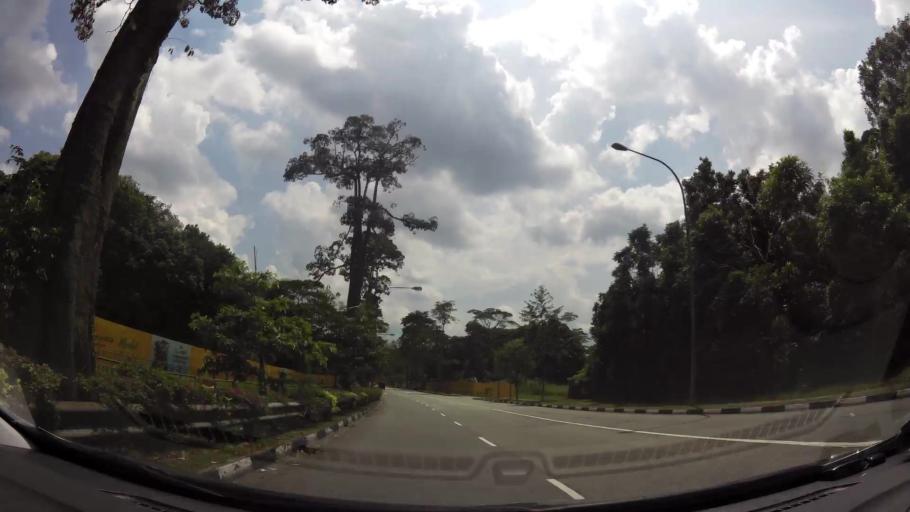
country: MY
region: Johor
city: Johor Bahru
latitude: 1.4102
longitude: 103.7788
